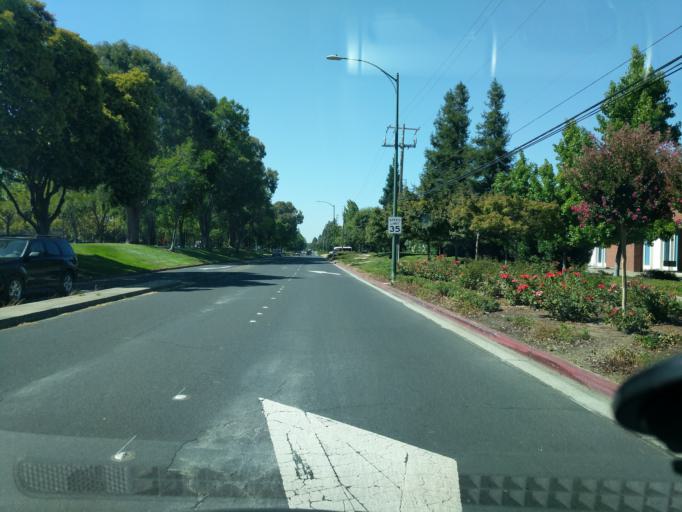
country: US
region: California
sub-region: Contra Costa County
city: Waldon
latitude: 37.9243
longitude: -122.0268
